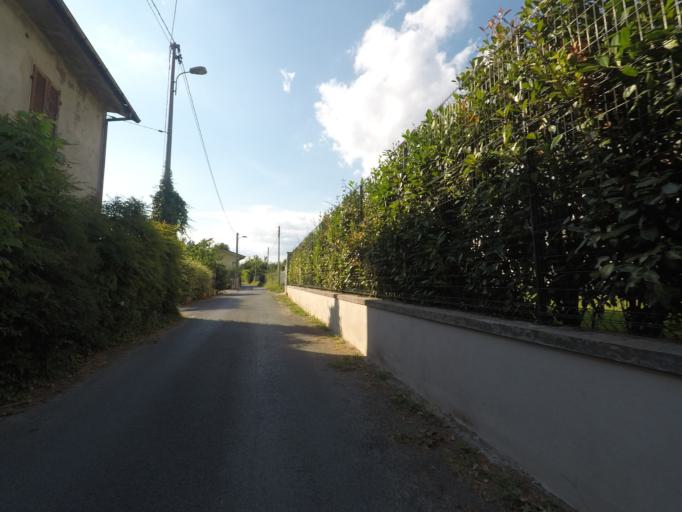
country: IT
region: Tuscany
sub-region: Provincia di Massa-Carrara
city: Capanne-Prato-Cinquale
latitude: 44.0121
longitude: 10.1466
